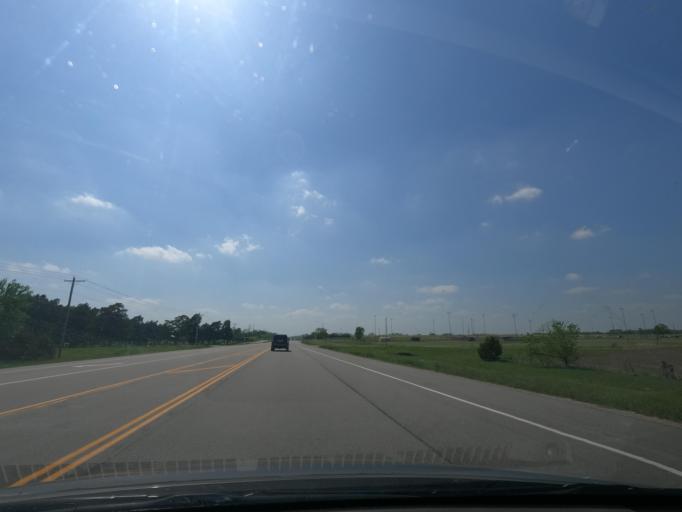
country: US
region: Kansas
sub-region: Butler County
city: El Dorado
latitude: 37.6796
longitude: -96.7856
